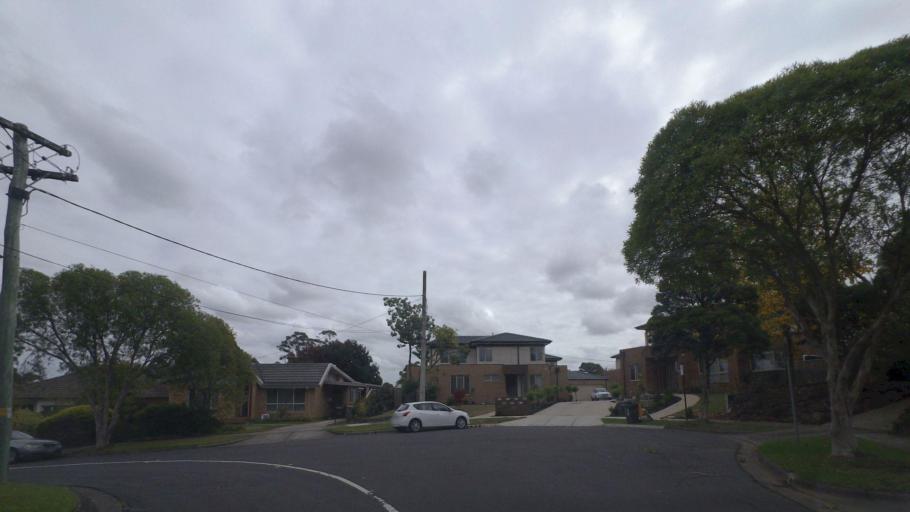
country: AU
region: Victoria
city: Forest Hill
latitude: -37.8284
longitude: 145.1824
